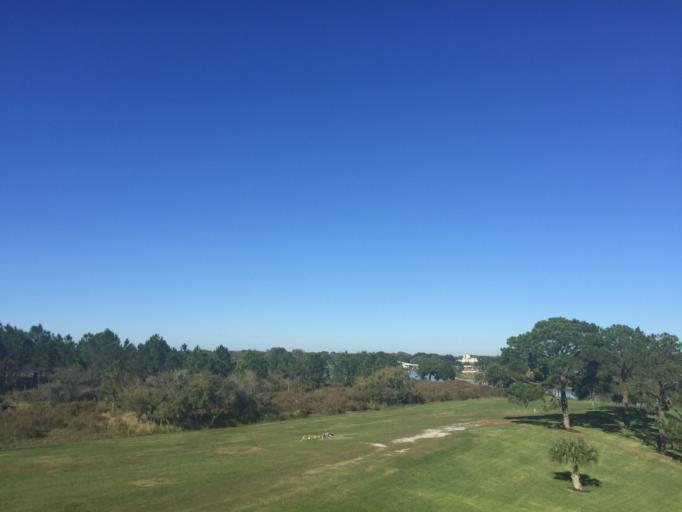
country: US
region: Florida
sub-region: Orange County
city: Bay Hill
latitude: 28.4115
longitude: -81.5755
